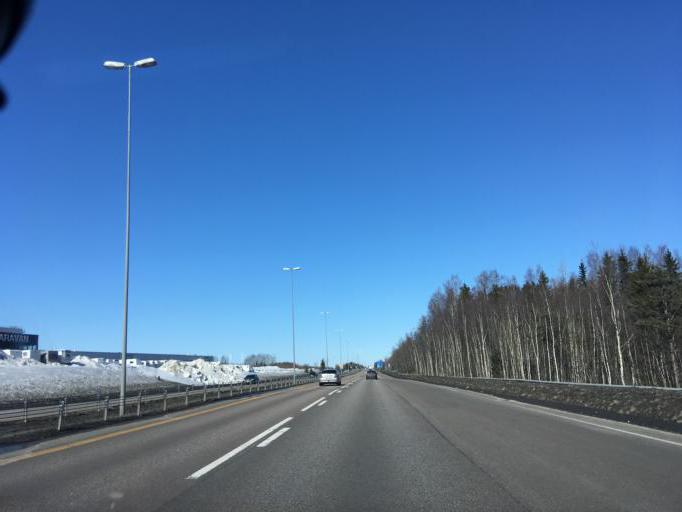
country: NO
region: Akershus
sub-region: Ullensaker
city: Klofta
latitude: 60.0840
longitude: 11.1490
